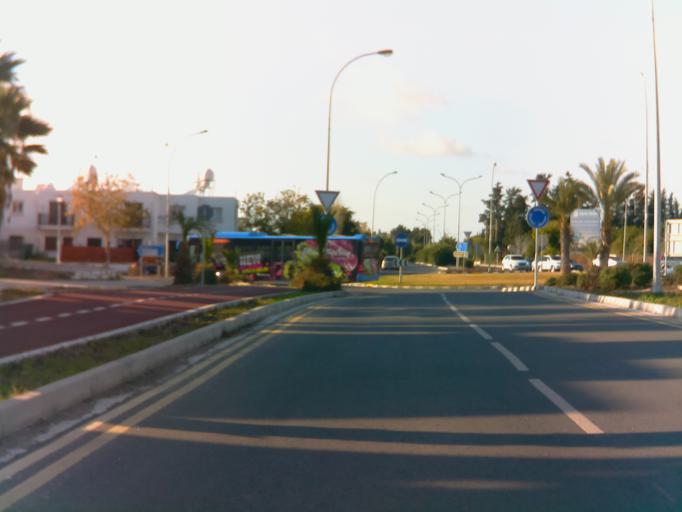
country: CY
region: Pafos
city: Paphos
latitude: 34.7512
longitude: 32.4298
